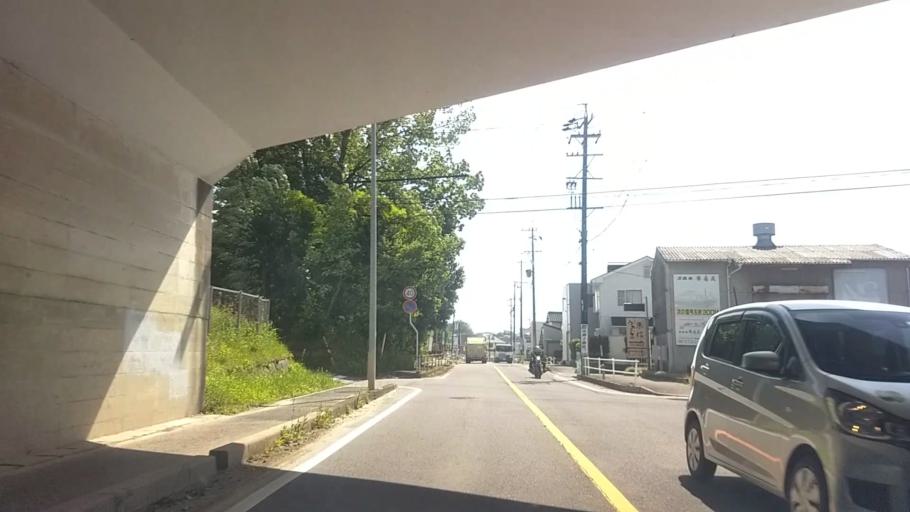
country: JP
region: Aichi
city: Okazaki
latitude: 34.9701
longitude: 137.1845
